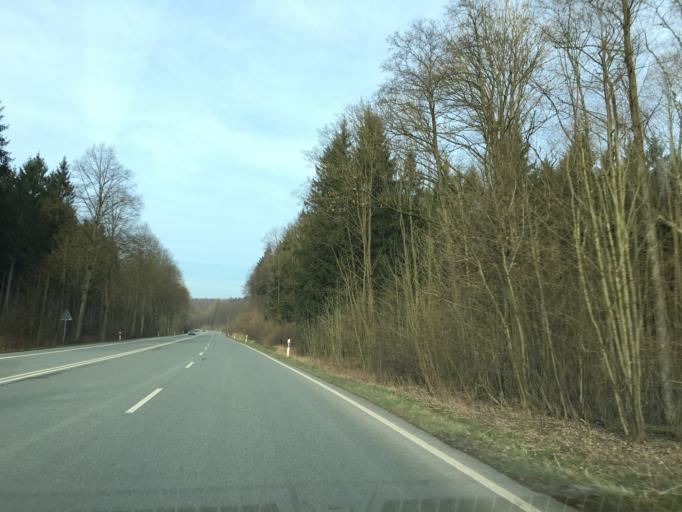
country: DE
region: North Rhine-Westphalia
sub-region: Regierungsbezirk Detmold
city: Willebadessen
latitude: 51.5534
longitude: 9.0142
